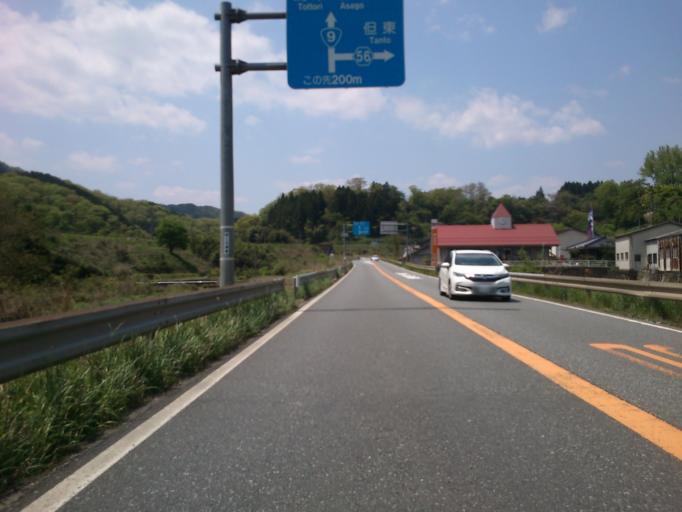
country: JP
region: Kyoto
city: Fukuchiyama
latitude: 35.3285
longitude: 134.9491
